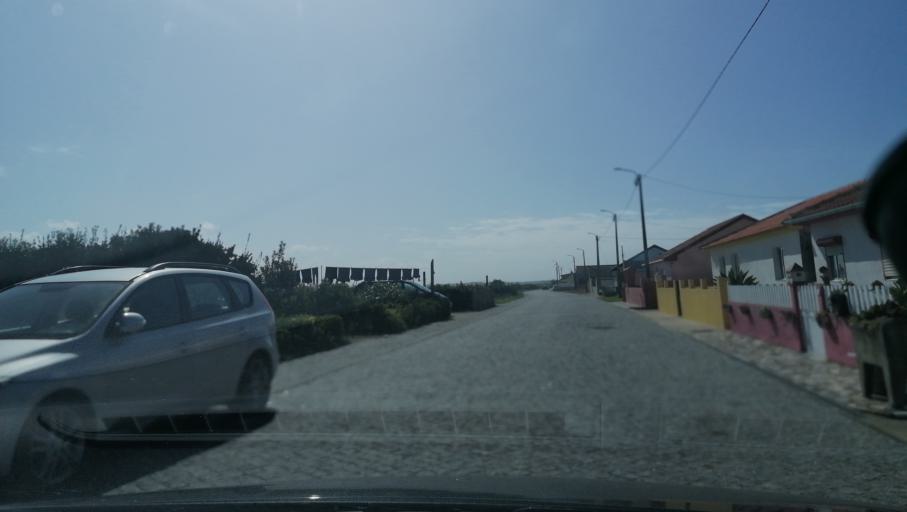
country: PT
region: Aveiro
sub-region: Espinho
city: Silvalde
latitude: 40.9803
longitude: -8.6469
